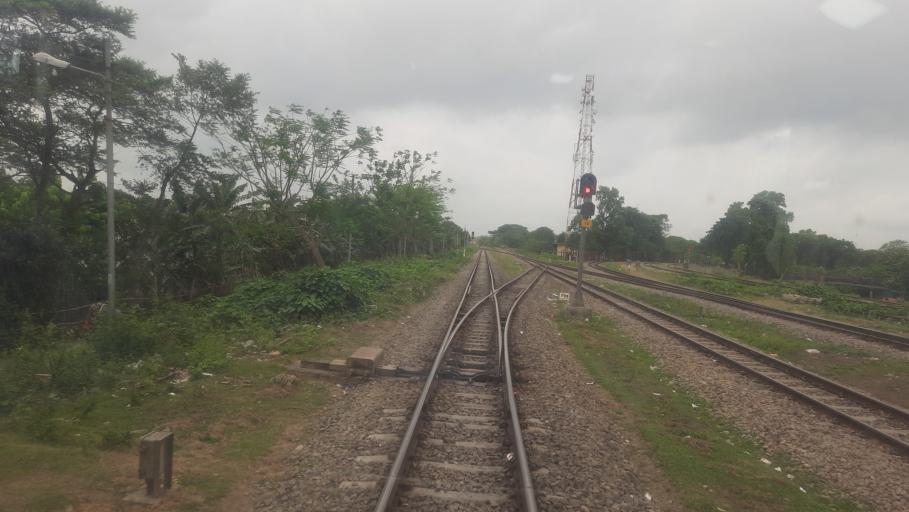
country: BD
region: Dhaka
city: Bhairab Bazar
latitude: 24.0503
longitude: 90.9756
